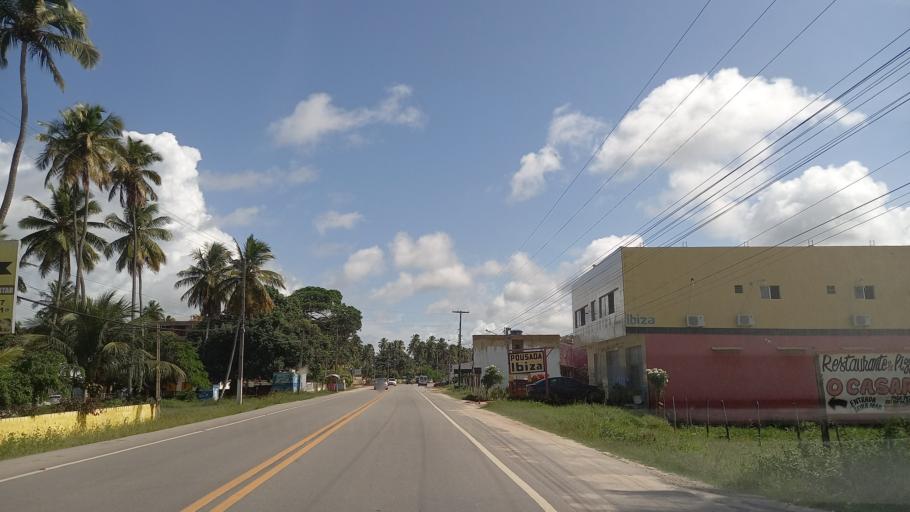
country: BR
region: Pernambuco
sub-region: Sao Jose Da Coroa Grande
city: Sao Jose da Coroa Grande
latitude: -8.9257
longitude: -35.1612
